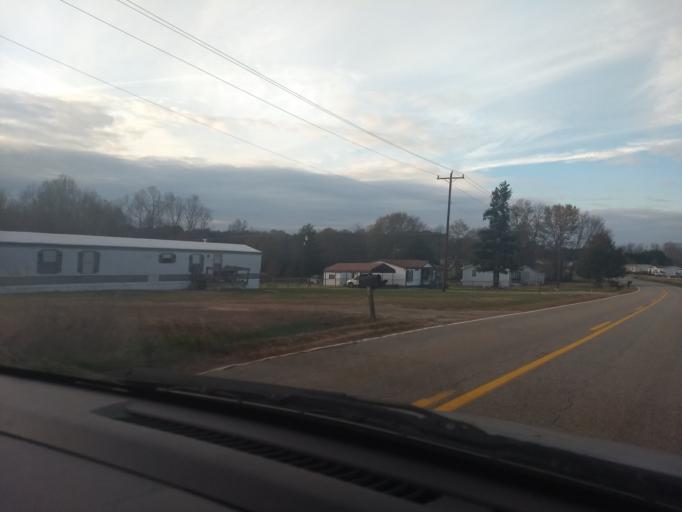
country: US
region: South Carolina
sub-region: Greenville County
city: Greer
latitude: 34.9906
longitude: -82.2027
